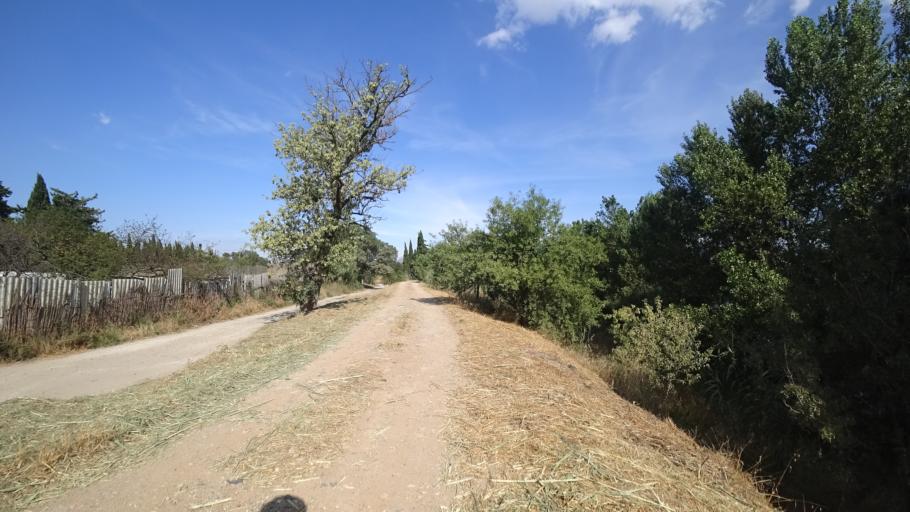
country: FR
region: Languedoc-Roussillon
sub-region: Departement des Pyrenees-Orientales
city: Rivesaltes
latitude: 42.7729
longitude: 2.8682
